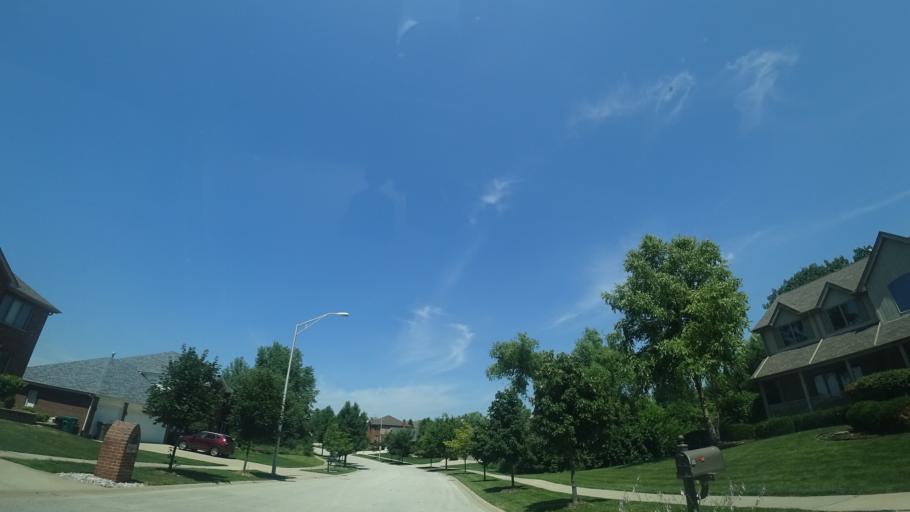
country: US
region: Illinois
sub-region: Will County
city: Mokena
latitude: 41.5574
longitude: -87.9041
